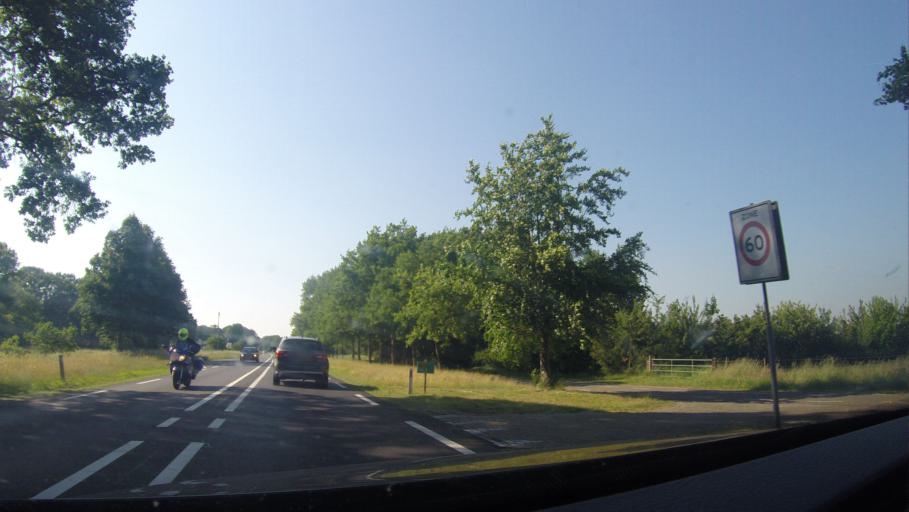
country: NL
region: Overijssel
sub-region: Gemeente Raalte
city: Heino
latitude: 52.4219
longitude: 6.2452
